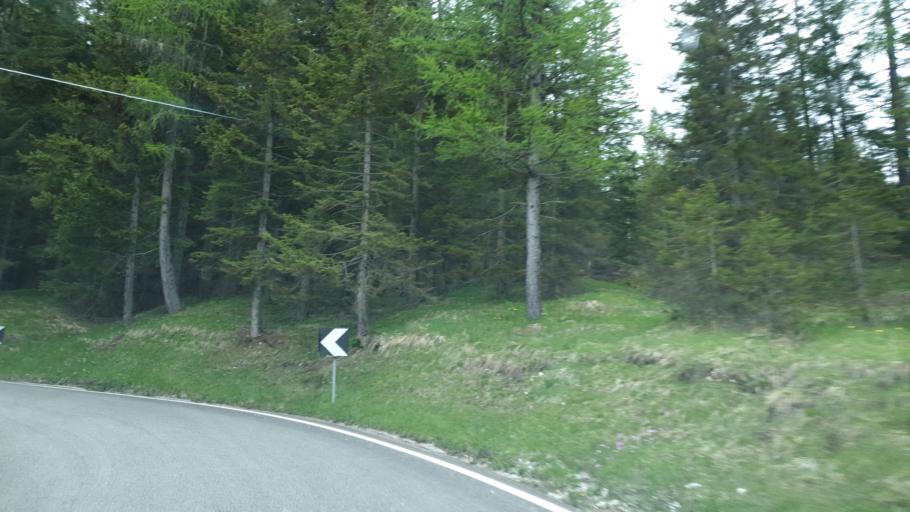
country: IT
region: Veneto
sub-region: Provincia di Belluno
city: San Vito
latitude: 46.5642
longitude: 12.2460
